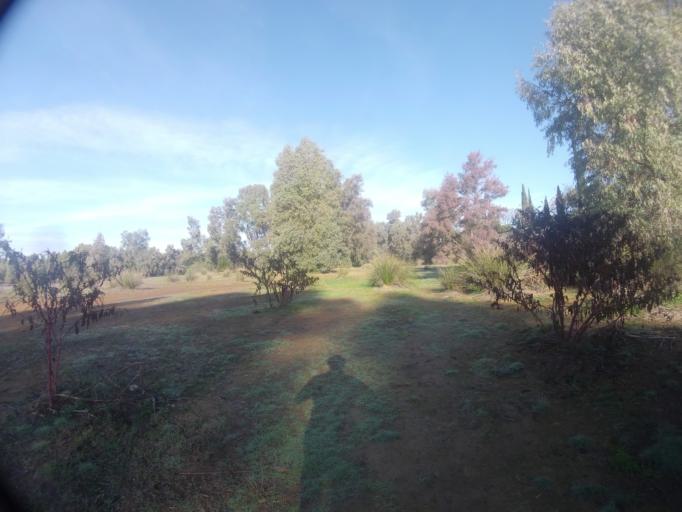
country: ES
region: Andalusia
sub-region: Provincia de Huelva
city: Gibraleon
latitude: 37.3747
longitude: -6.9760
